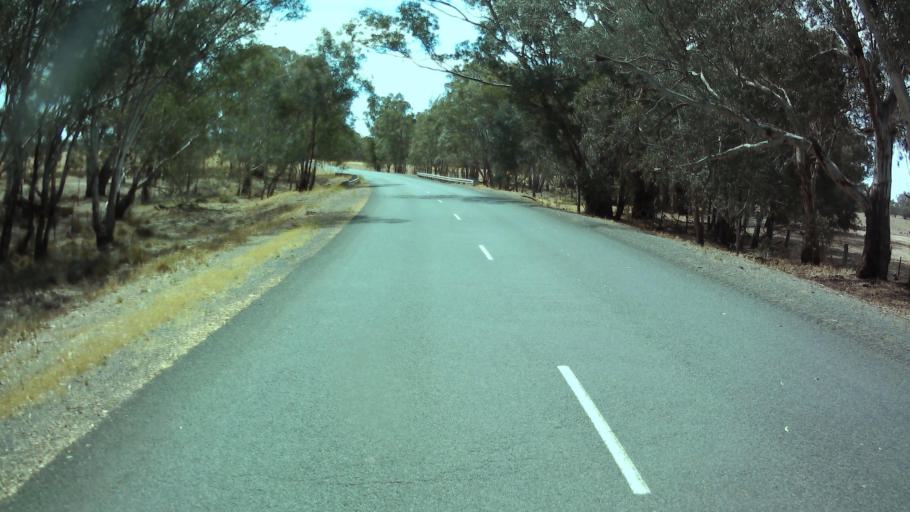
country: AU
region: New South Wales
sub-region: Weddin
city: Grenfell
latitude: -33.7932
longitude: 148.2151
